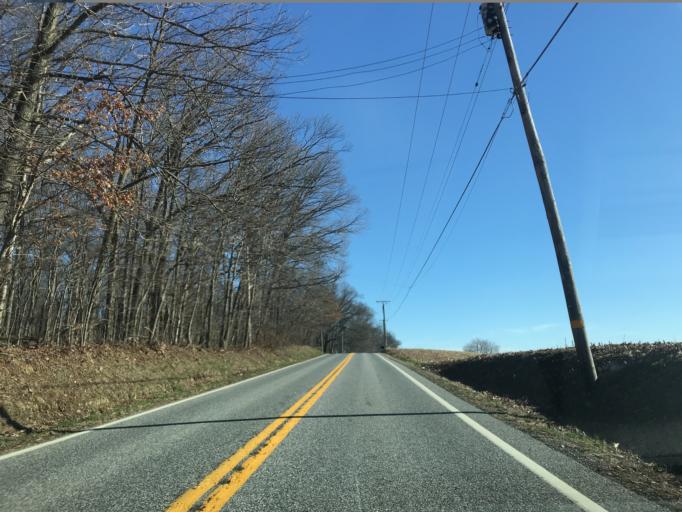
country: US
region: Maryland
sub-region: Harford County
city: Jarrettsville
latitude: 39.6554
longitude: -76.5481
